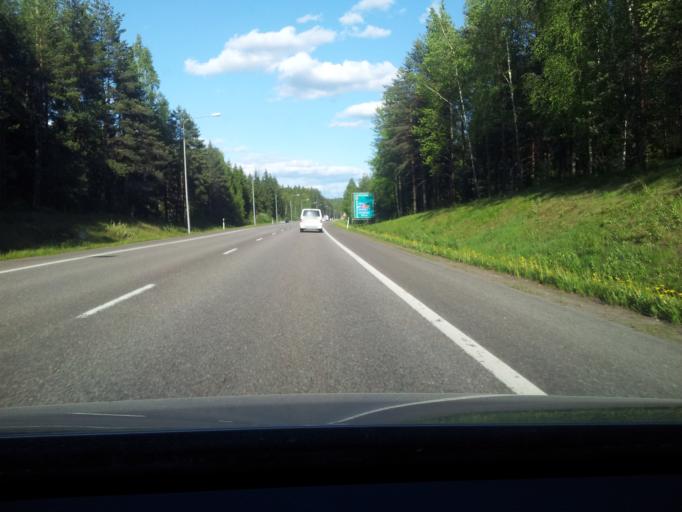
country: FI
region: Kymenlaakso
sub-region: Kouvola
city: Kouvola
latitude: 60.8849
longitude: 26.7444
